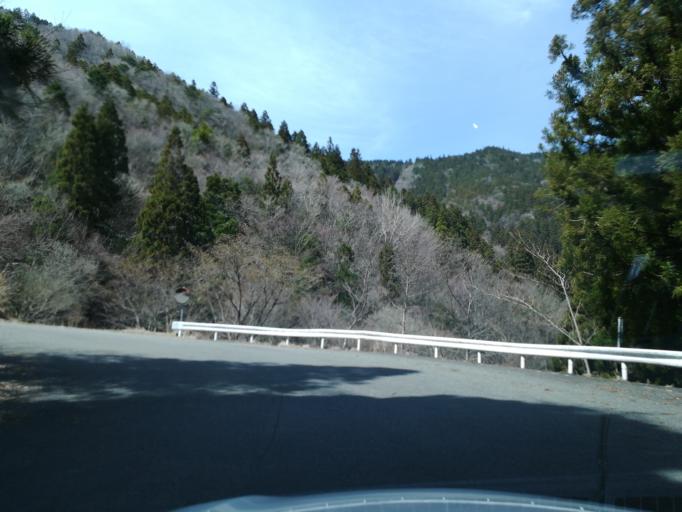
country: JP
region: Tokushima
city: Wakimachi
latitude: 33.8850
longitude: 134.0473
